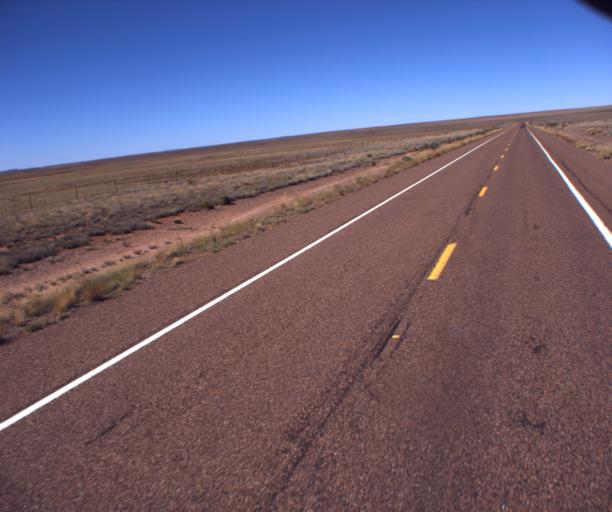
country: US
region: Arizona
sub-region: Navajo County
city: Holbrook
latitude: 34.8254
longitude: -109.9315
